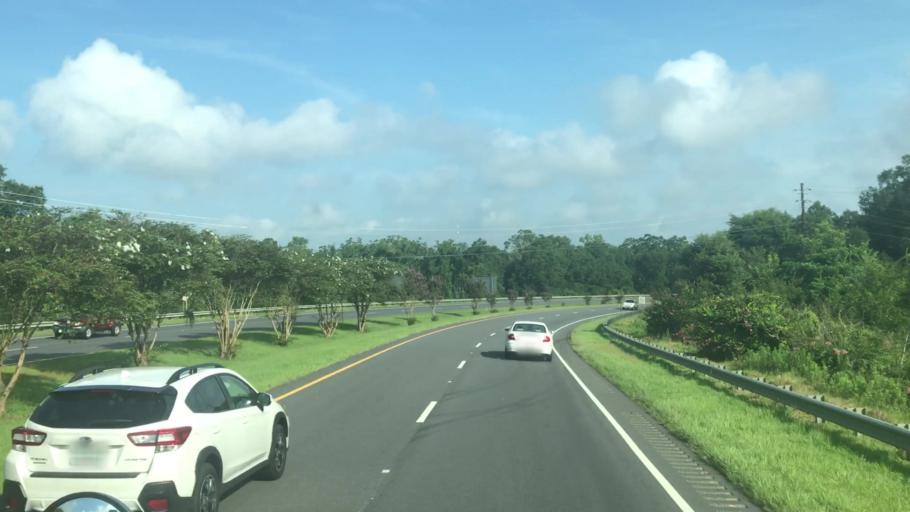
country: US
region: Georgia
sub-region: Decatur County
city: Bainbridge
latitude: 30.8980
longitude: -84.5862
